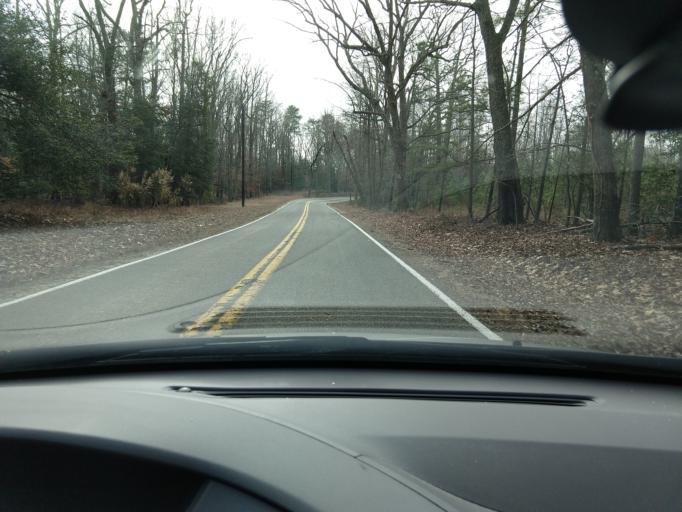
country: US
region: Virginia
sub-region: Henrico County
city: Fort Lee
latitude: 37.4280
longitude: -77.2386
